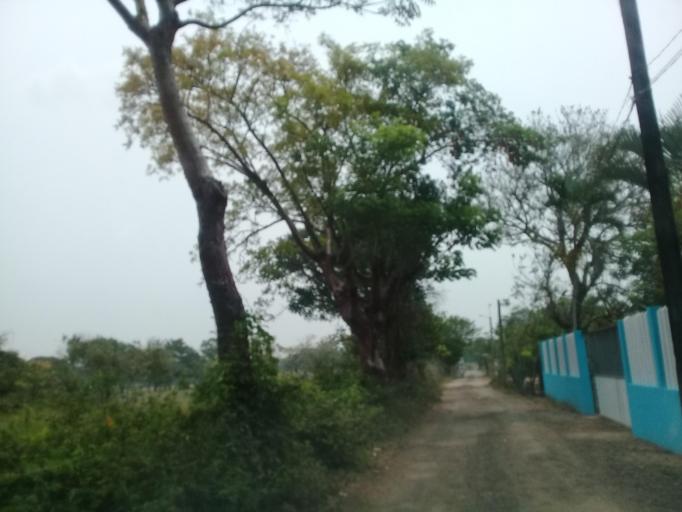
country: MX
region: Veracruz
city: Jamapa
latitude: 18.9555
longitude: -96.1971
